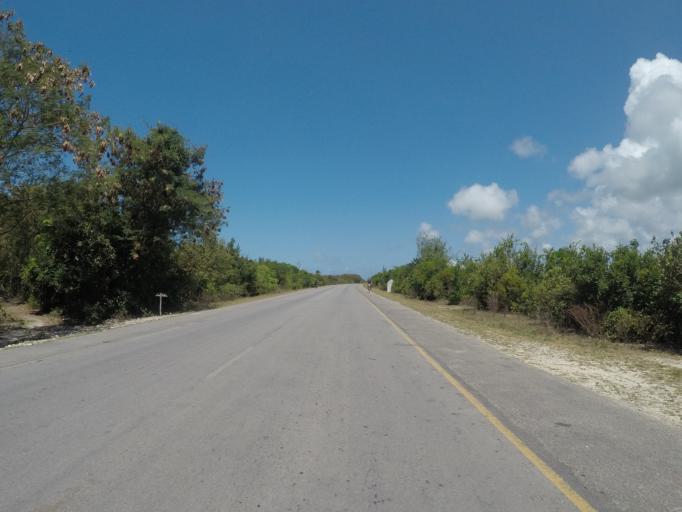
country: TZ
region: Zanzibar Central/South
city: Nganane
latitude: -6.3241
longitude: 39.5457
